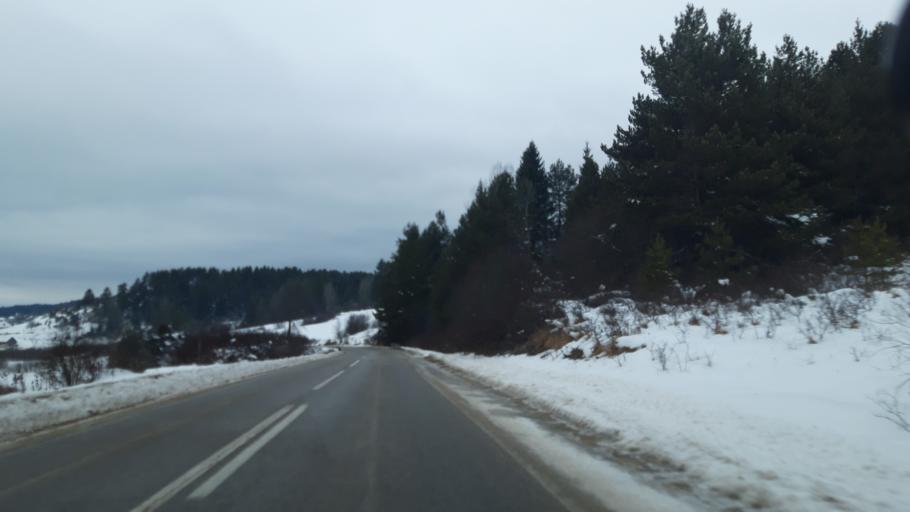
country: BA
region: Republika Srpska
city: Han Pijesak
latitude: 44.0037
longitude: 18.8868
